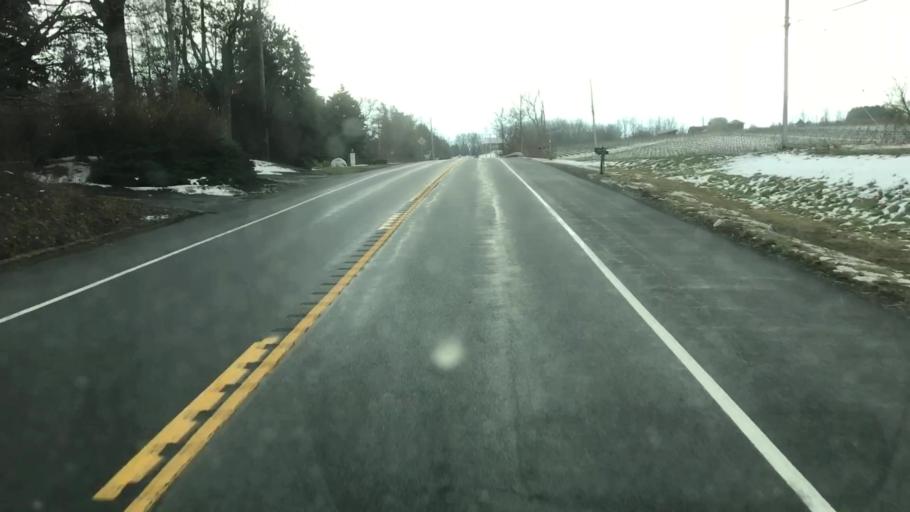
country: US
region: New York
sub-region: Onondaga County
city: Skaneateles
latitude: 42.8939
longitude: -76.4172
